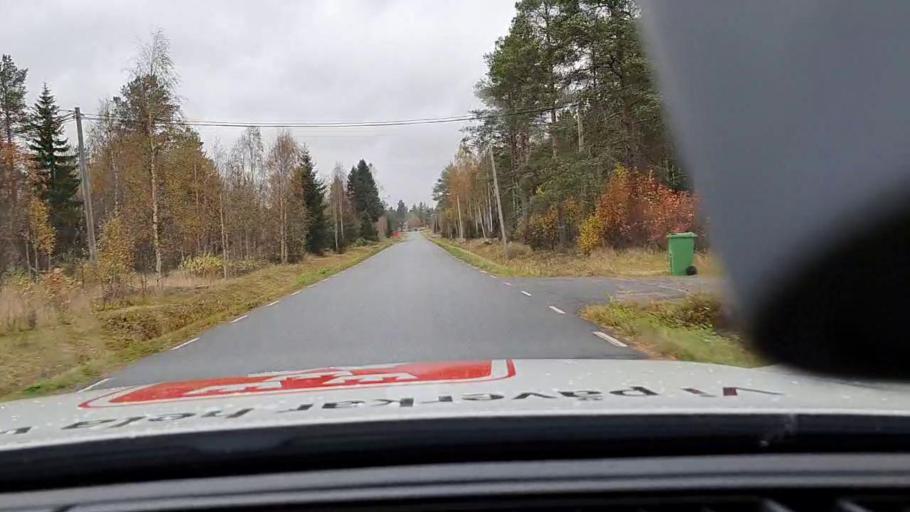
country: SE
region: Norrbotten
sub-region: Haparanda Kommun
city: Haparanda
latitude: 65.9448
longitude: 23.7998
